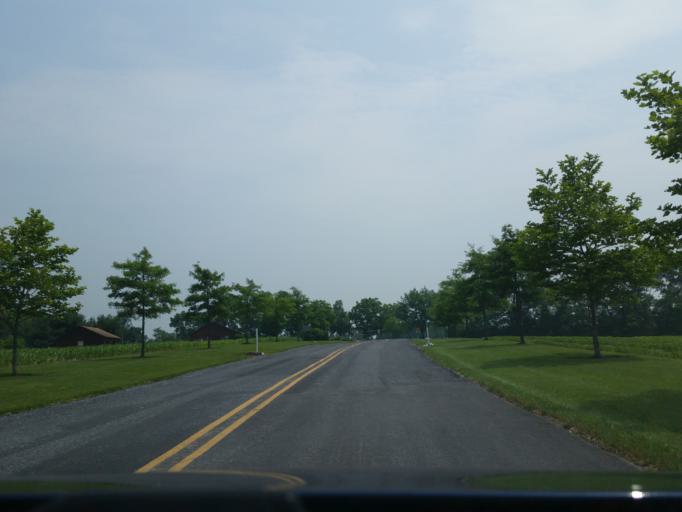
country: US
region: Pennsylvania
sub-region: Lebanon County
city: Palmyra
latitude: 40.4101
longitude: -76.6217
